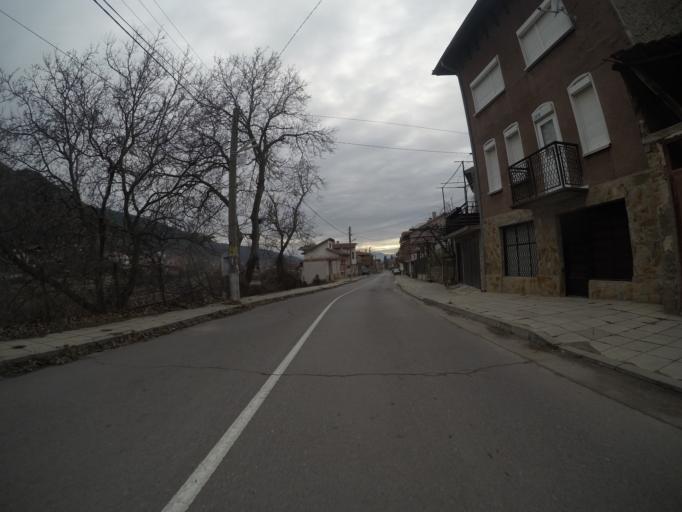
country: BG
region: Kyustendil
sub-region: Obshtina Rila
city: Rila
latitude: 42.1300
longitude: 23.1368
